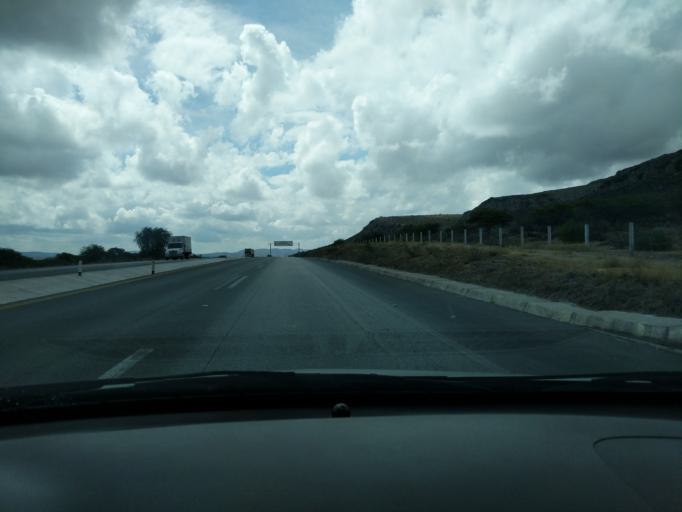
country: MX
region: Zacatecas
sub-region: Pinos
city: Santiago
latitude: 22.4006
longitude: -101.3752
